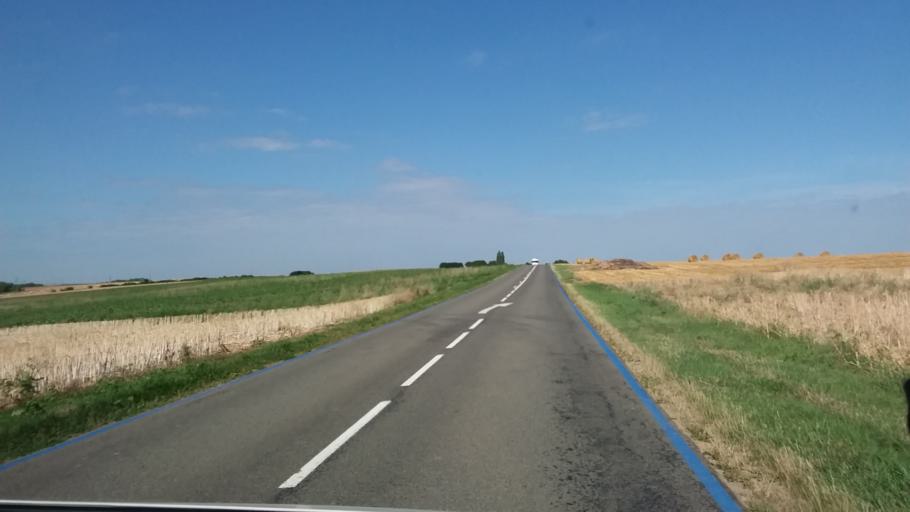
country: FR
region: Picardie
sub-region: Departement de l'Aisne
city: Bruyeres-et-Montberault
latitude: 49.4413
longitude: 3.6834
